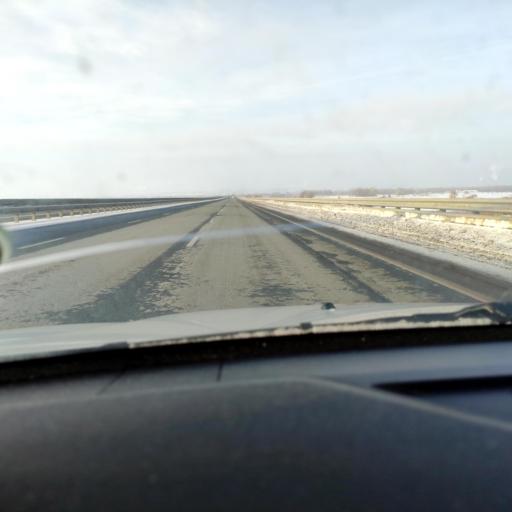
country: RU
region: Samara
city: Smyshlyayevka
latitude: 53.1531
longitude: 50.3509
